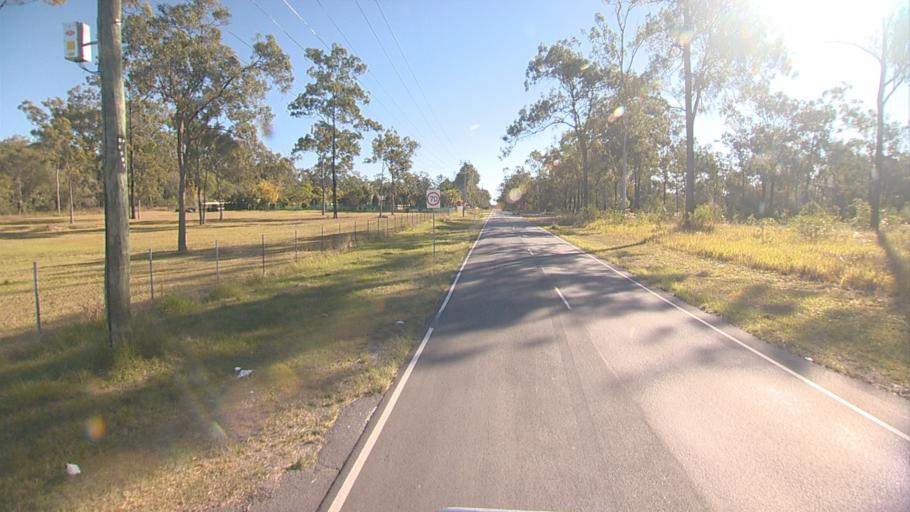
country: AU
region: Queensland
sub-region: Logan
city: Park Ridge South
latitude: -27.7370
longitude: 153.0264
